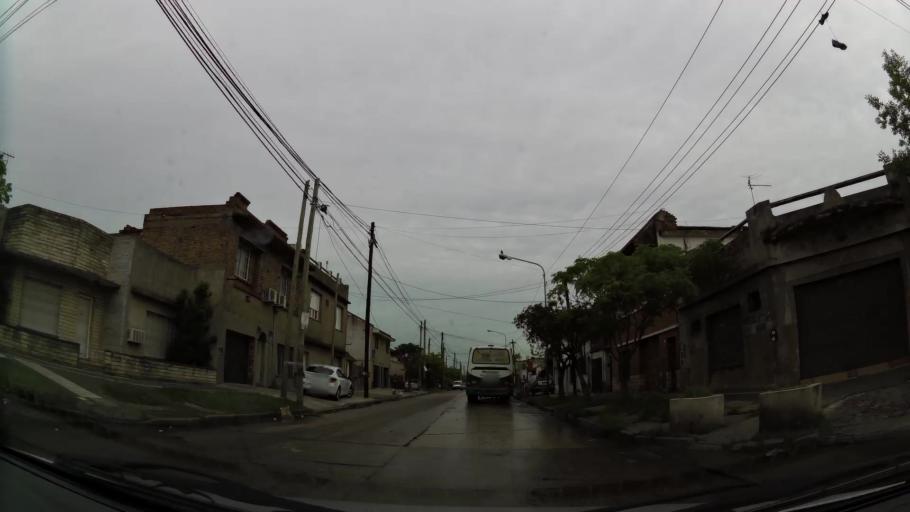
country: AR
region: Buenos Aires
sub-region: Partido de Lanus
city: Lanus
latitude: -34.7143
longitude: -58.3687
